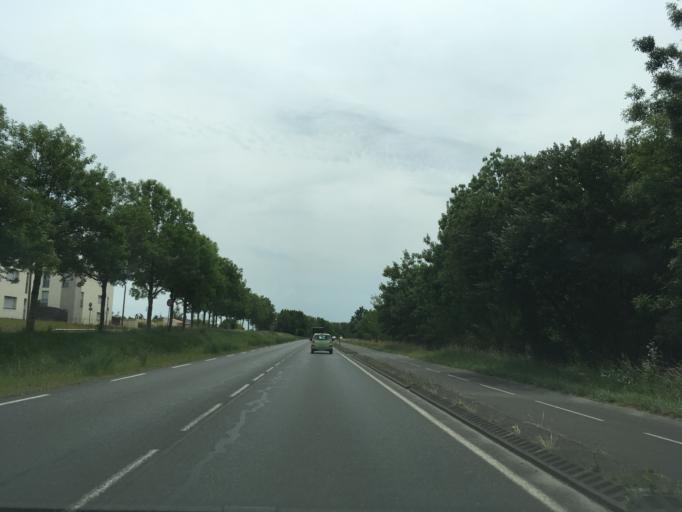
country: FR
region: Poitou-Charentes
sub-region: Departement des Deux-Sevres
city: Niort
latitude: 46.3242
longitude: -0.4894
